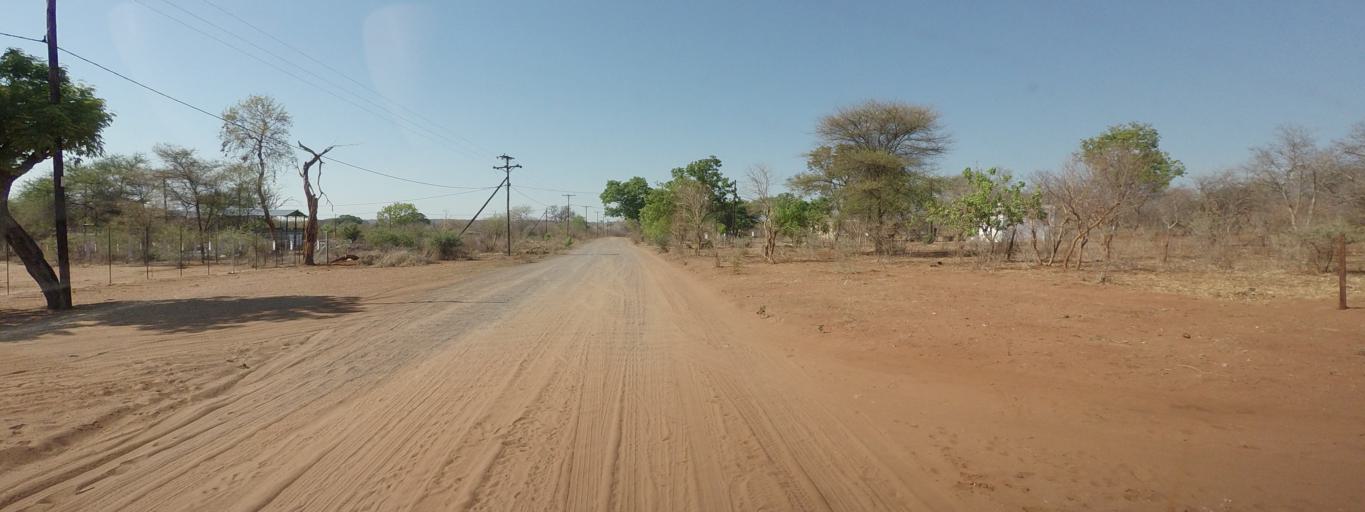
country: BW
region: North West
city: Kasane
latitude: -17.8944
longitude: 25.2290
